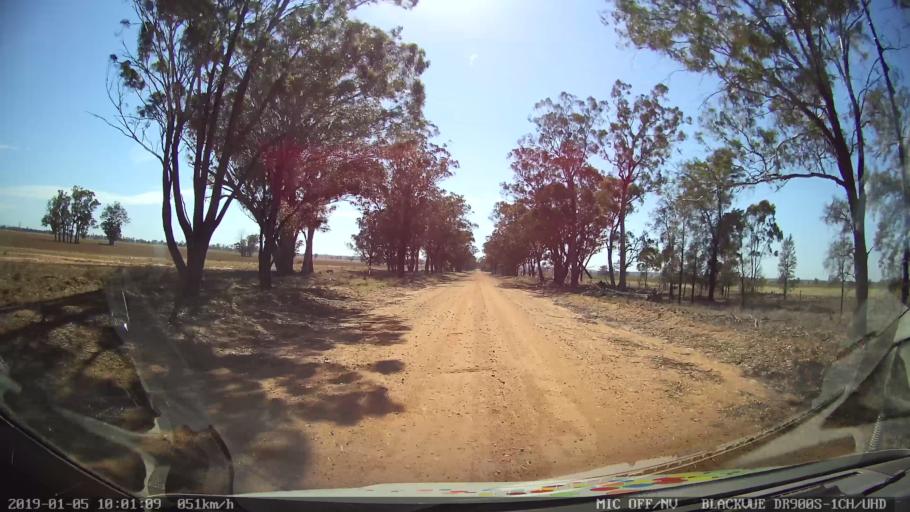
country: AU
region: New South Wales
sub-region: Gilgandra
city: Gilgandra
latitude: -31.6694
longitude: 148.8334
